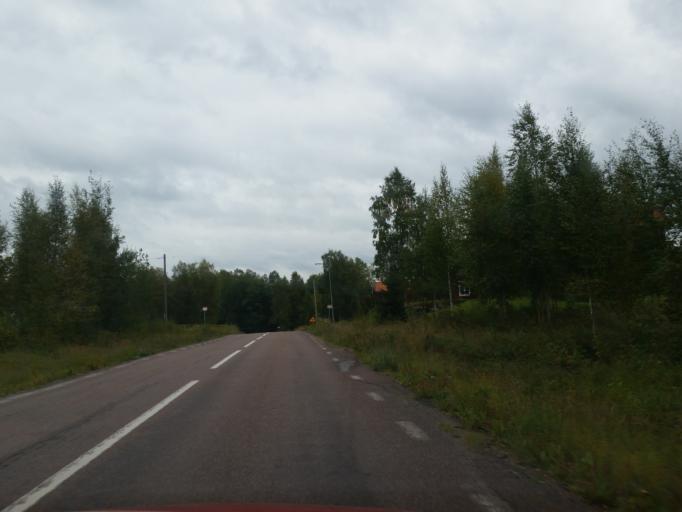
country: SE
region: Dalarna
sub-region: Gagnefs Kommun
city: Gagnef
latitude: 60.6686
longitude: 15.1519
